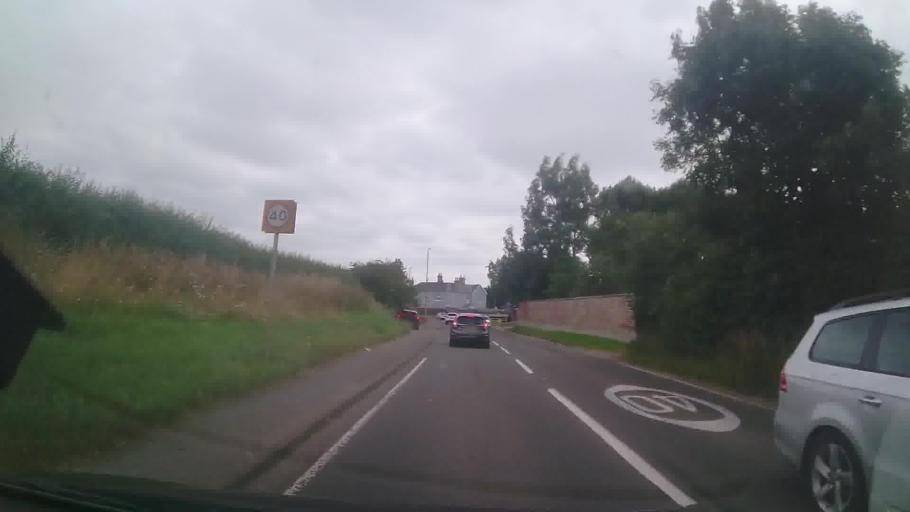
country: GB
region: England
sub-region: Leicestershire
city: Desford
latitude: 52.6349
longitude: -1.2790
